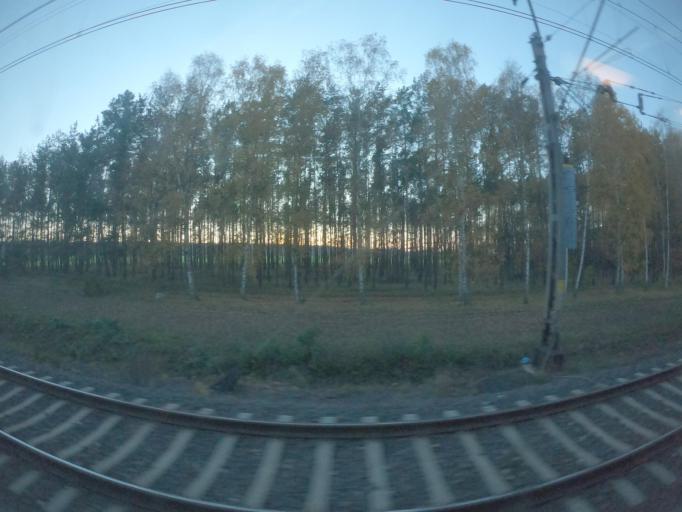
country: PL
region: West Pomeranian Voivodeship
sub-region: Powiat mysliborski
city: Boleszkowice
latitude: 52.7327
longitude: 14.5213
